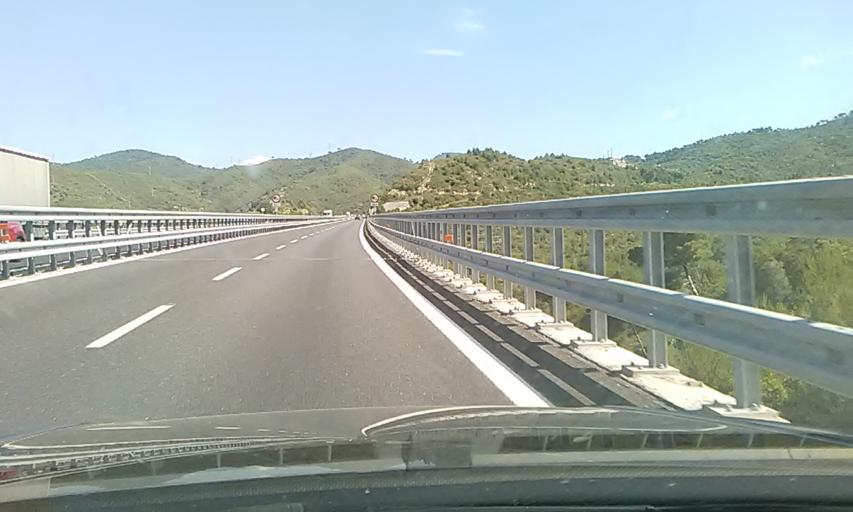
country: IT
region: Liguria
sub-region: Provincia di Savona
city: Laigueglia
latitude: 43.9852
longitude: 8.1364
